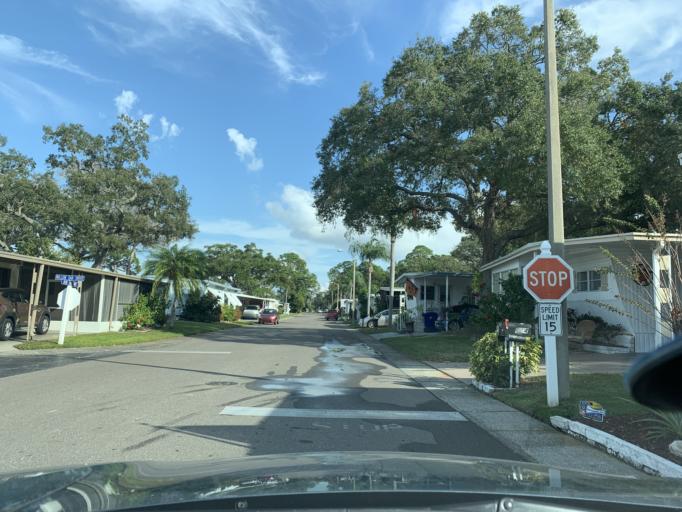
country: US
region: Florida
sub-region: Pinellas County
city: Largo
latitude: 27.8996
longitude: -82.7812
